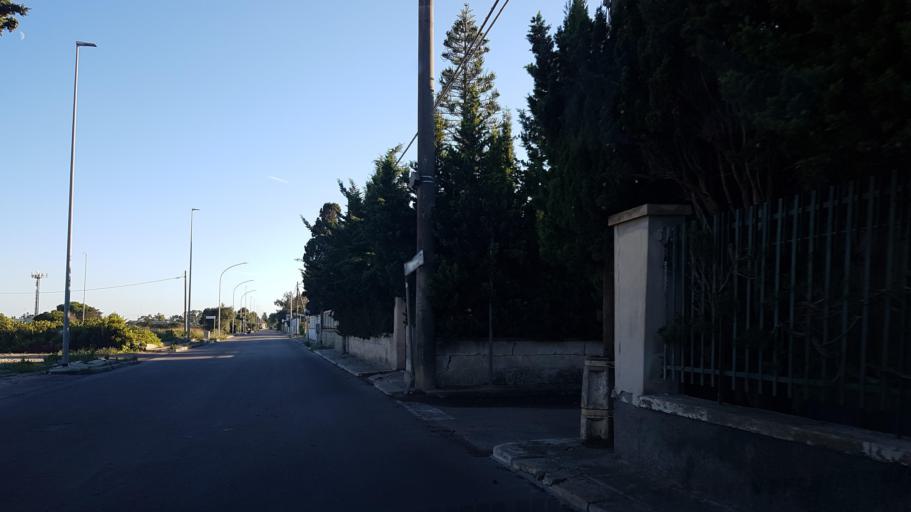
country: IT
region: Apulia
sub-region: Provincia di Lecce
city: Giorgilorio
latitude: 40.4623
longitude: 18.1951
